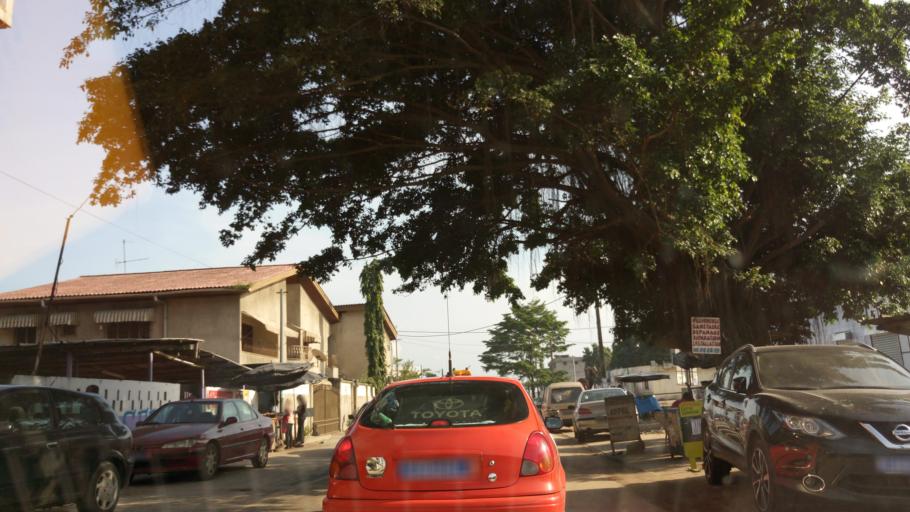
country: CI
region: Lagunes
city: Abobo
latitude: 5.3721
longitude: -3.9575
